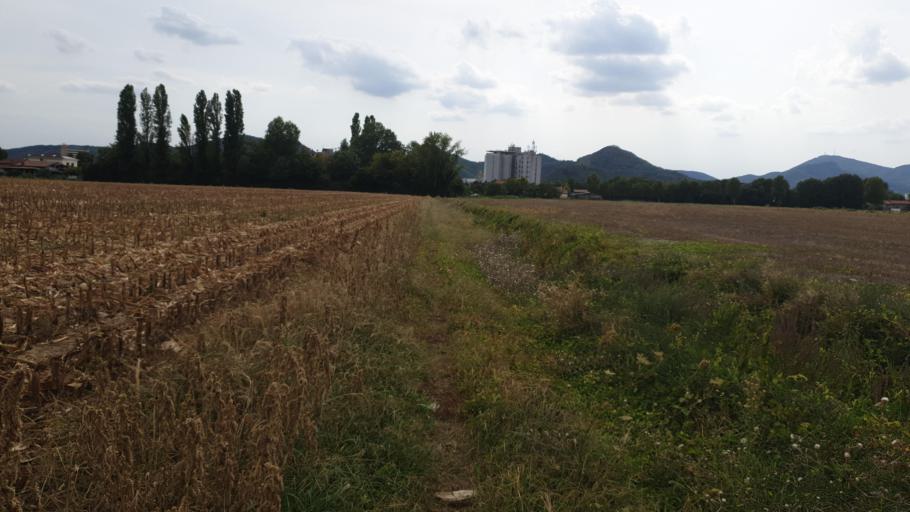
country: IT
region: Veneto
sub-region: Provincia di Padova
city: Montegrotto Terme
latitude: 45.3382
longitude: 11.7974
